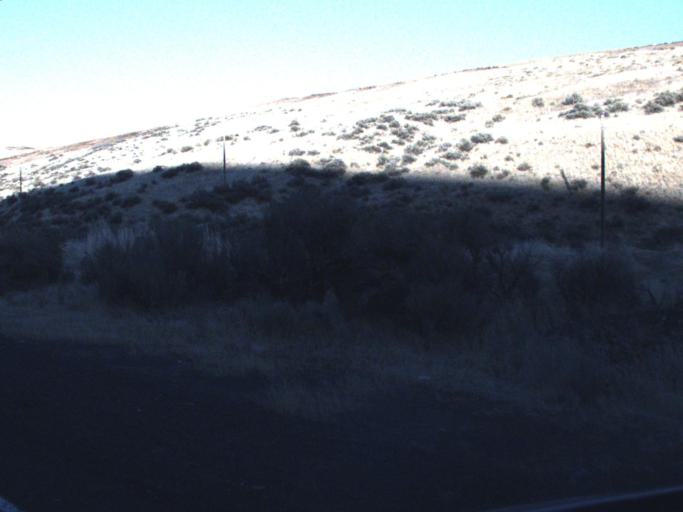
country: US
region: Washington
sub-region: Franklin County
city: Connell
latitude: 46.6745
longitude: -118.5442
